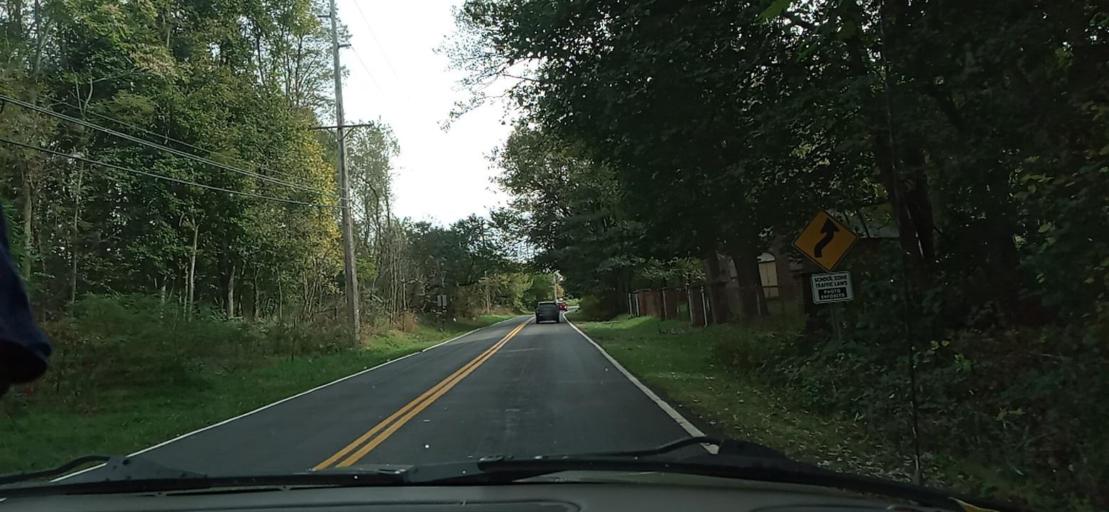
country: US
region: Ohio
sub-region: Summit County
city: Portage Lakes
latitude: 41.0206
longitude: -81.5138
